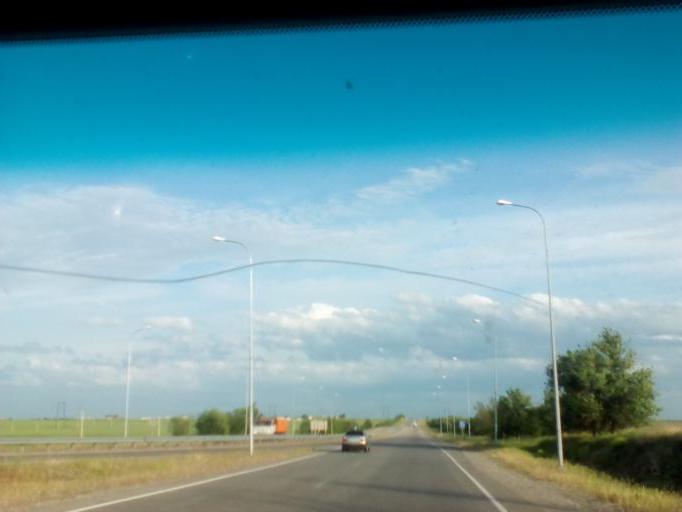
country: KZ
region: Ongtustik Qazaqstan
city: Temirlanovka
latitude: 42.5255
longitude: 69.3438
